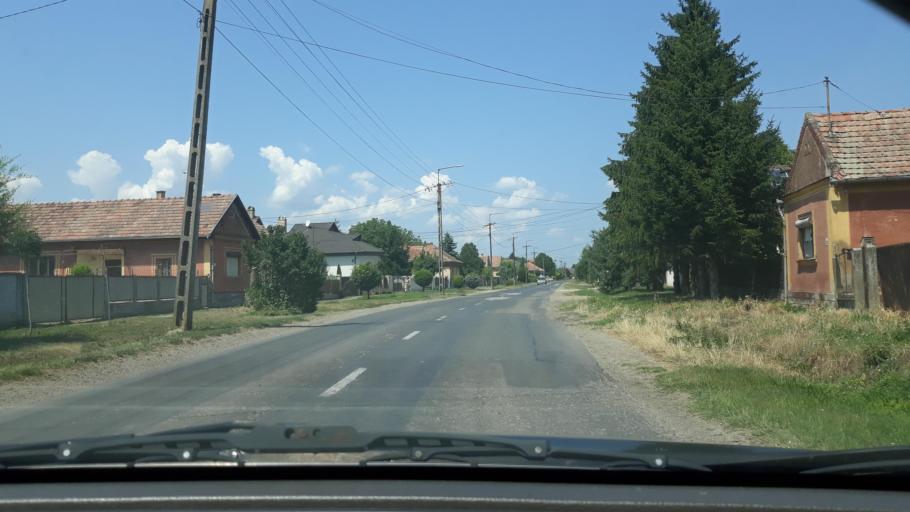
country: HU
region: Hajdu-Bihar
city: Hosszupalyi
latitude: 47.3873
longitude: 21.7339
